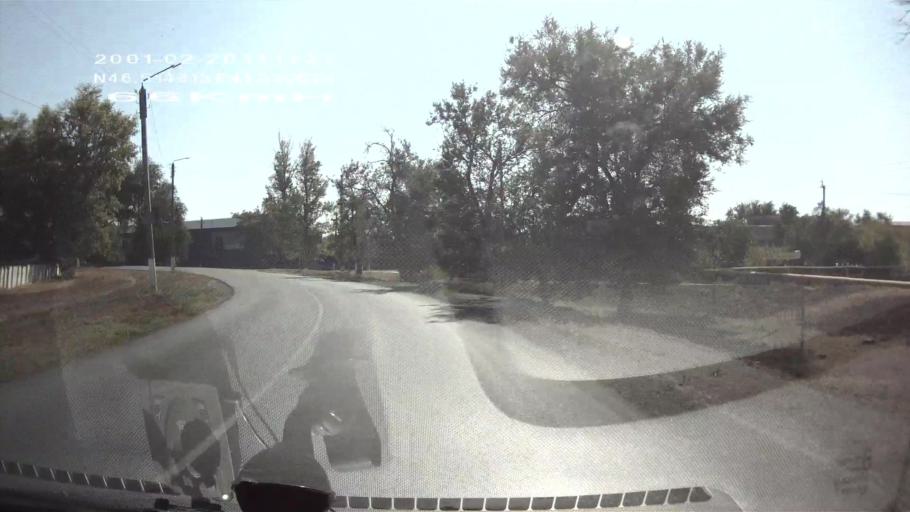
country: RU
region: Rostov
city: Gigant
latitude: 46.5146
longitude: 41.3307
